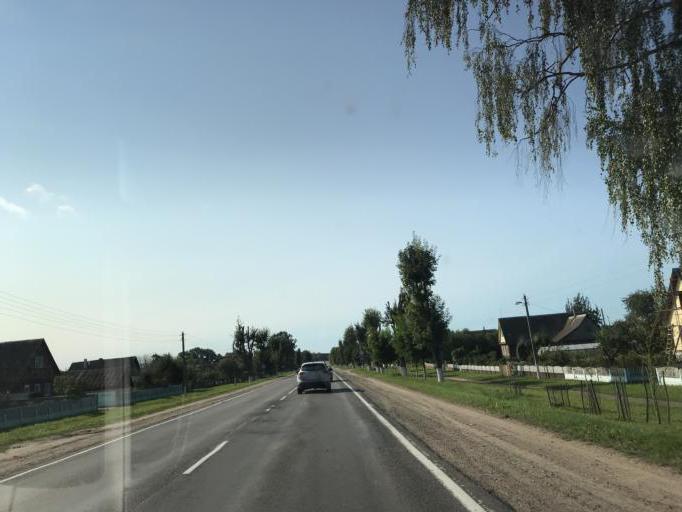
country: BY
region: Mogilev
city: Buynichy
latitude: 53.8343
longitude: 30.2455
